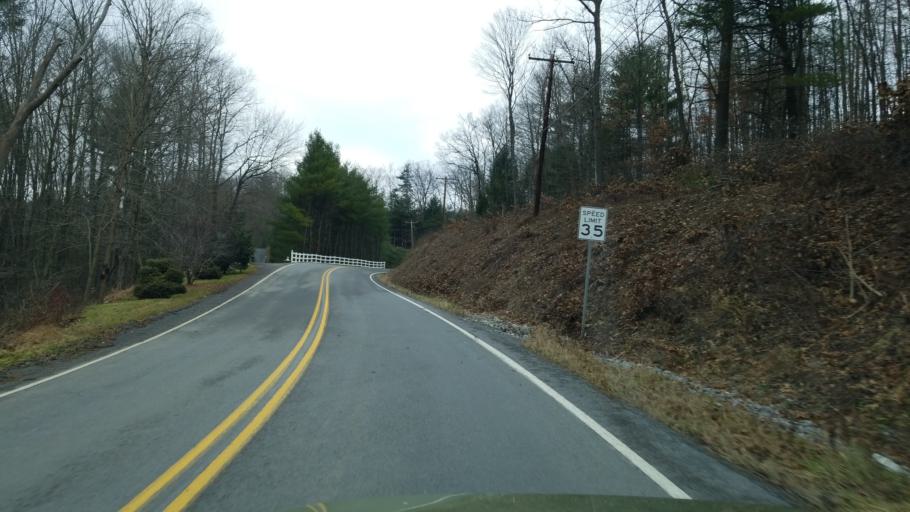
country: US
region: Pennsylvania
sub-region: Clearfield County
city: Clearfield
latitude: 41.0326
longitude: -78.4605
